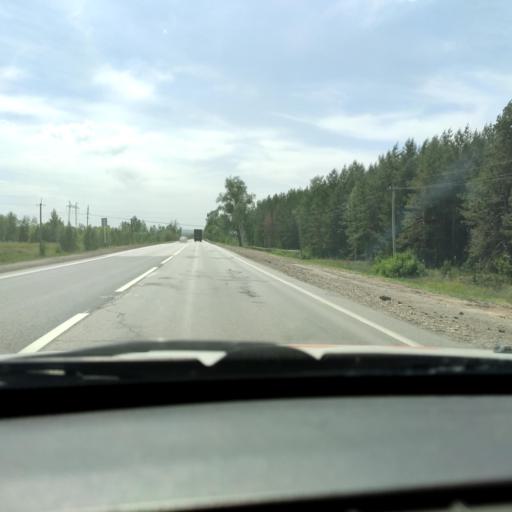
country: RU
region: Samara
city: Mirnyy
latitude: 53.5121
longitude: 50.3070
